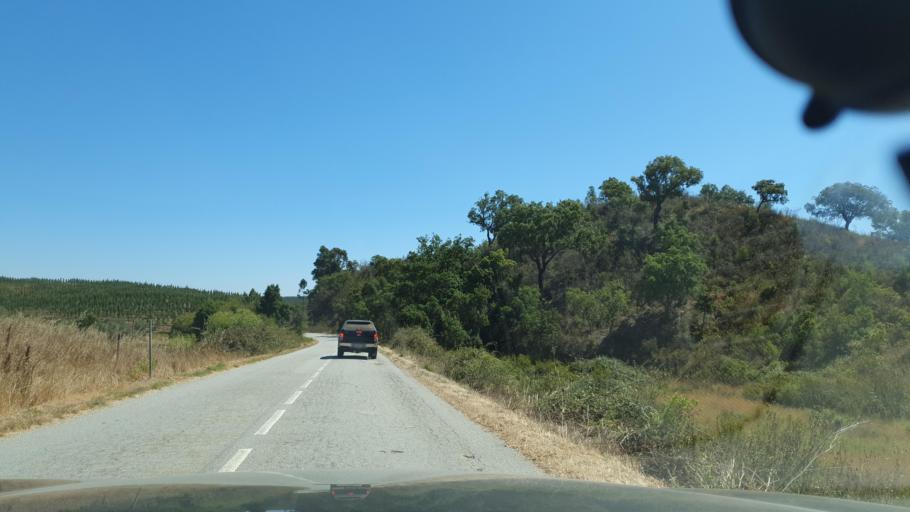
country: PT
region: Faro
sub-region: Monchique
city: Monchique
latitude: 37.4225
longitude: -8.5390
